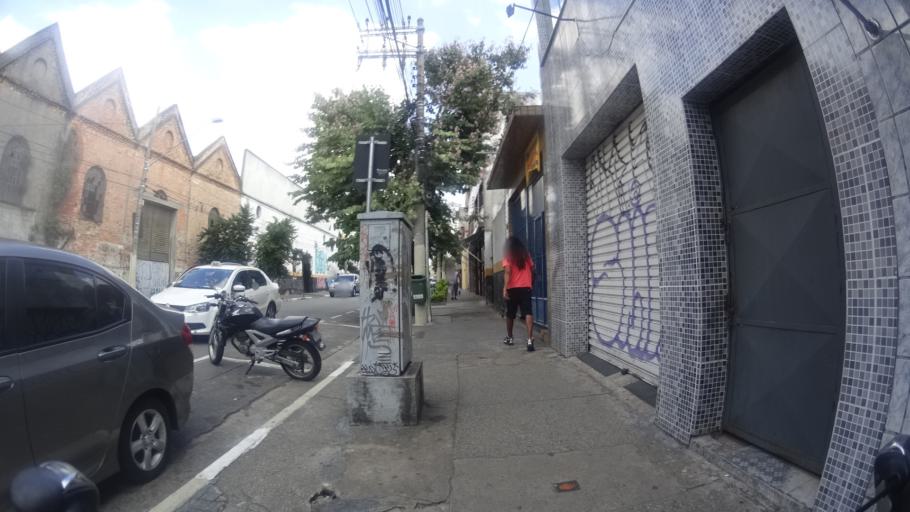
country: BR
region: Sao Paulo
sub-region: Sao Paulo
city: Sao Paulo
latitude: -23.5532
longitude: -46.6026
